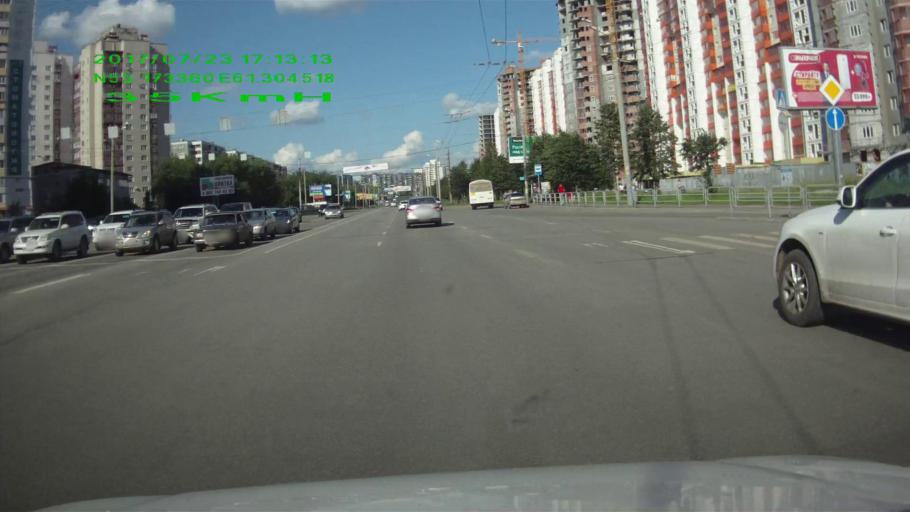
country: RU
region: Chelyabinsk
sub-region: Gorod Chelyabinsk
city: Chelyabinsk
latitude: 55.1736
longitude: 61.3050
